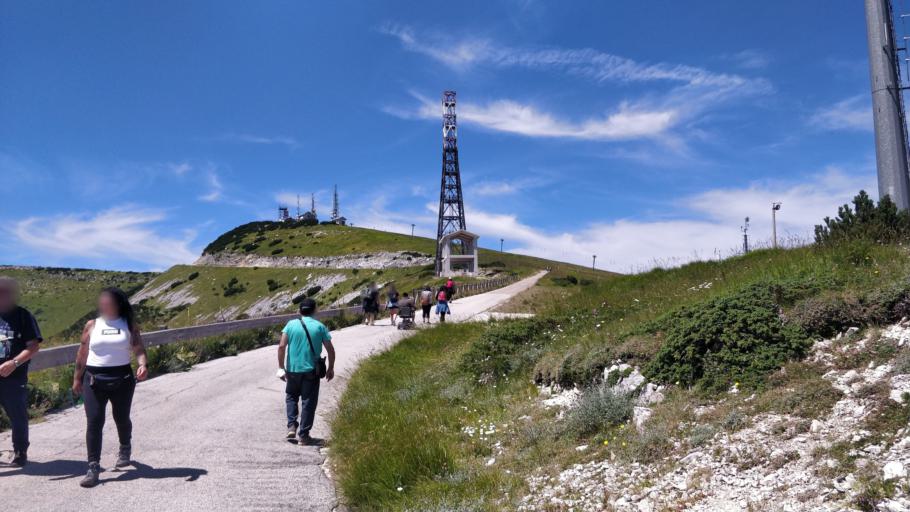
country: IT
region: Abruzzo
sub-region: Provincia di Chieti
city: Pennapiedimonte
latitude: 42.1585
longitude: 14.1332
